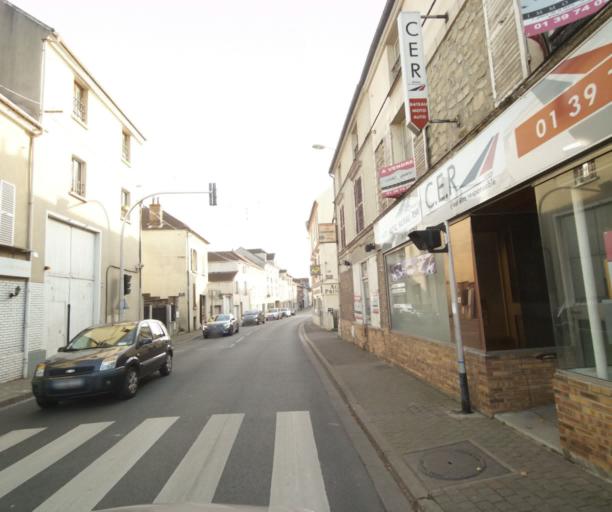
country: FR
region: Ile-de-France
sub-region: Departement des Yvelines
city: Triel-sur-Seine
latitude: 48.9790
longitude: 2.0042
